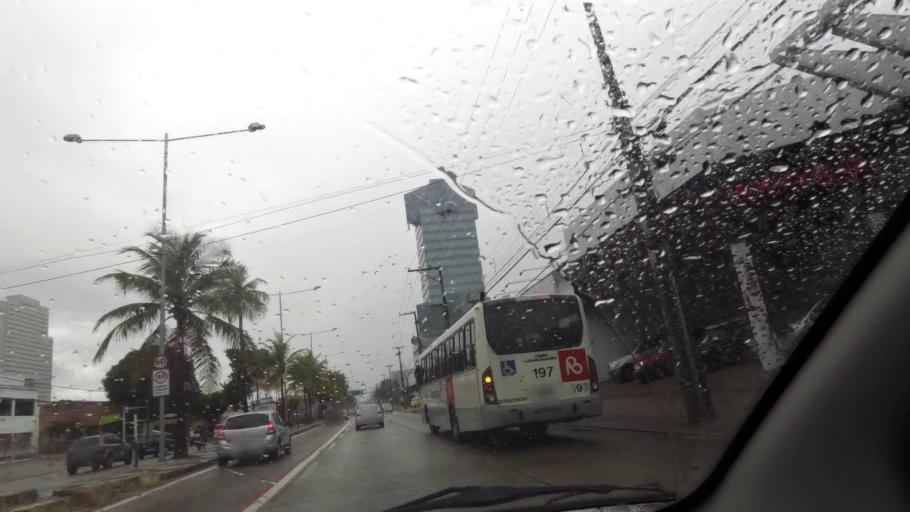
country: BR
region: Pernambuco
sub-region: Recife
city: Recife
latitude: -8.0867
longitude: -34.8854
